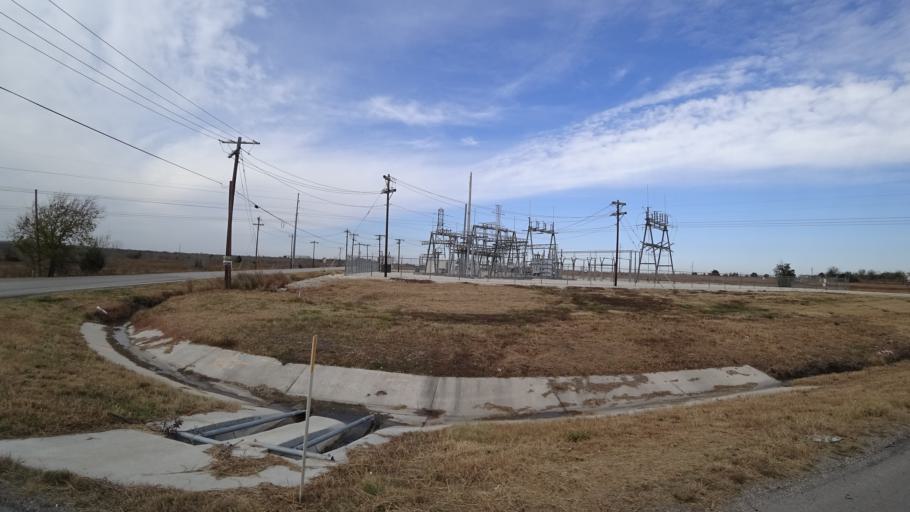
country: US
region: Texas
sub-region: Travis County
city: Onion Creek
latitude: 30.1384
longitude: -97.6786
